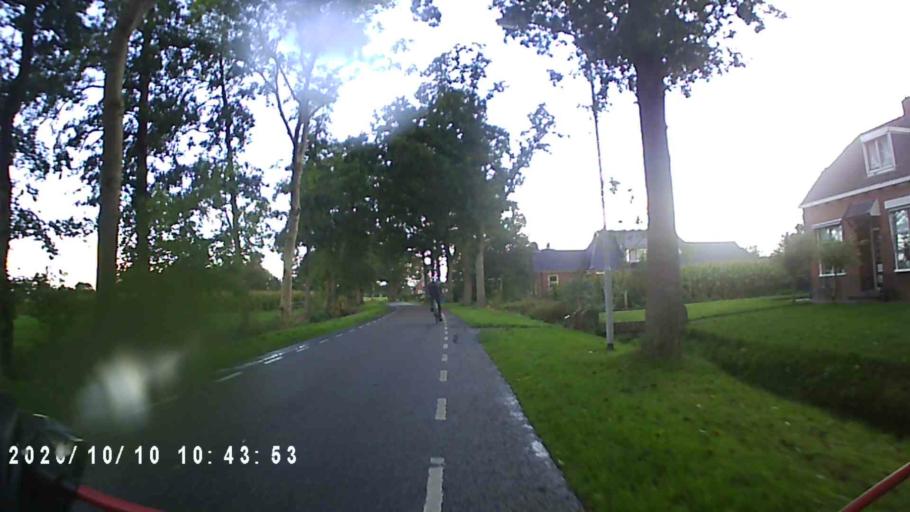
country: NL
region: Groningen
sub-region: Gemeente Grootegast
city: Grootegast
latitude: 53.1730
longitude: 6.2650
